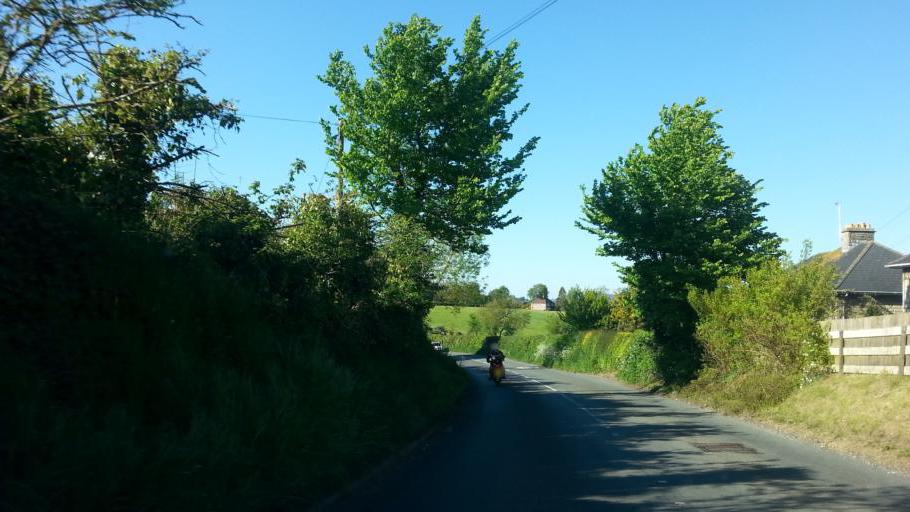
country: GB
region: England
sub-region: Somerset
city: Wincanton
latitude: 51.0265
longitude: -2.4395
